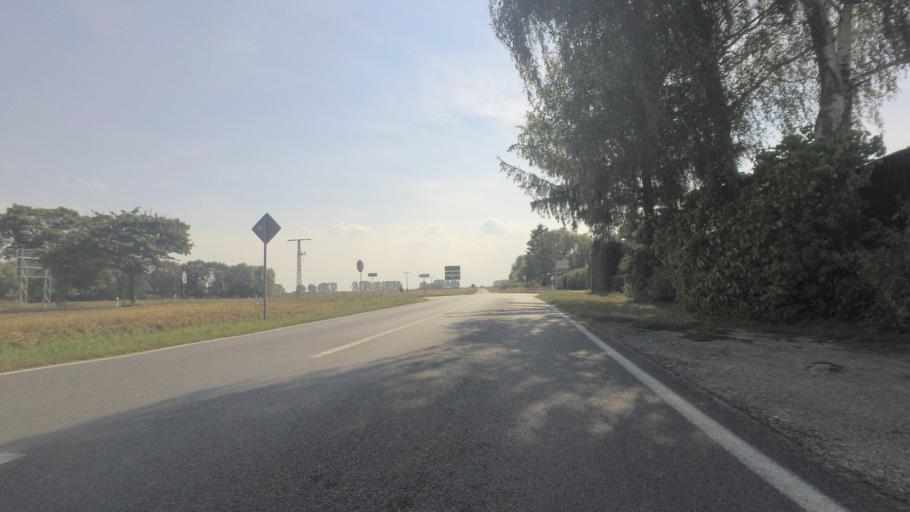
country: DE
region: Mecklenburg-Vorpommern
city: Wittenhagen
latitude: 54.1457
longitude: 13.1528
